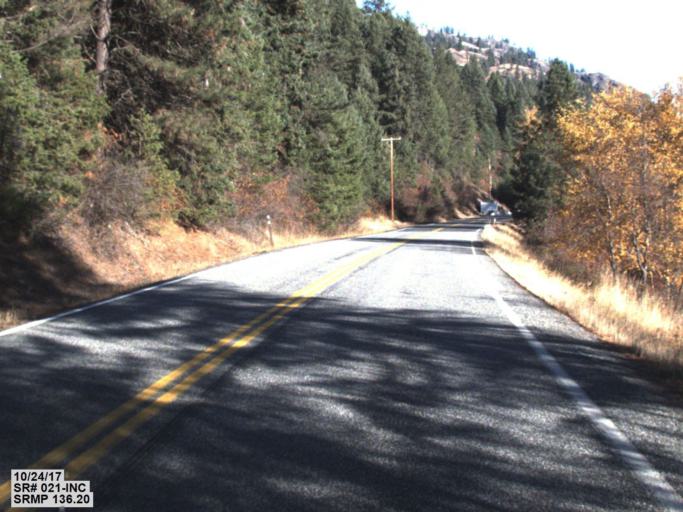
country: US
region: Washington
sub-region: Ferry County
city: Republic
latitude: 48.3373
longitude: -118.7493
